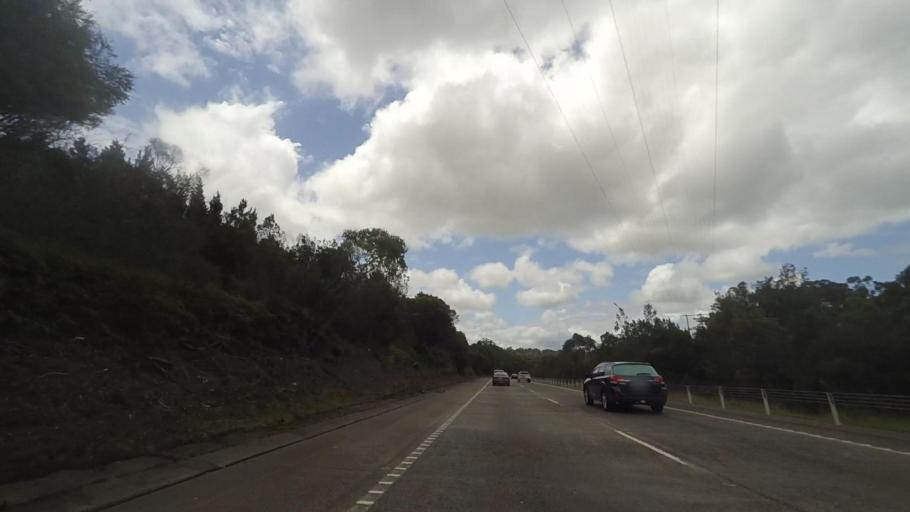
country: AU
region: New South Wales
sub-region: Gosford Shire
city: Narara
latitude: -33.3859
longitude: 151.2985
